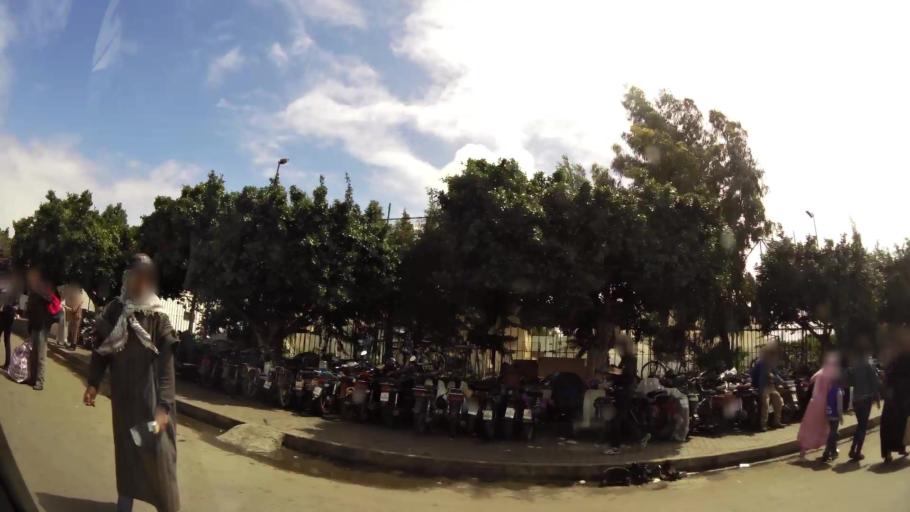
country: MA
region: Grand Casablanca
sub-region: Casablanca
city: Casablanca
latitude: 33.5752
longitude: -7.5876
